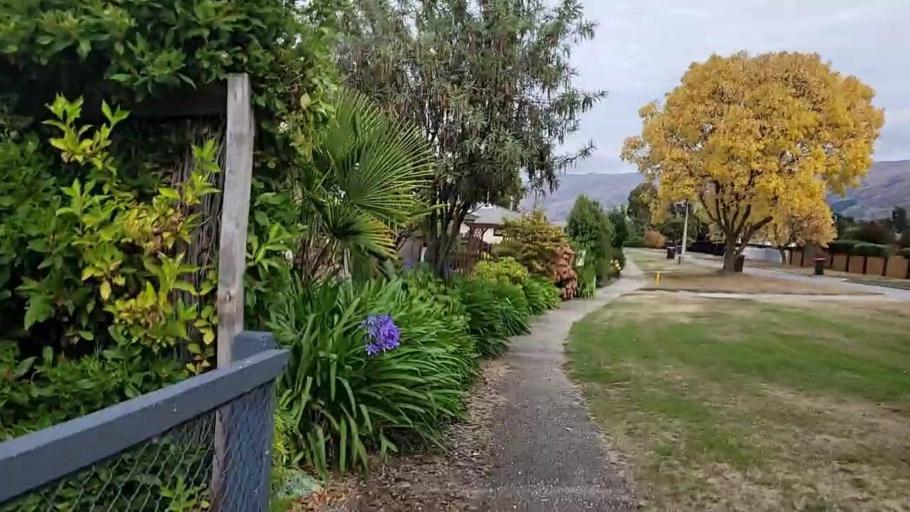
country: NZ
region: Otago
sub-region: Queenstown-Lakes District
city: Kingston
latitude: -45.4785
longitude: 169.3134
